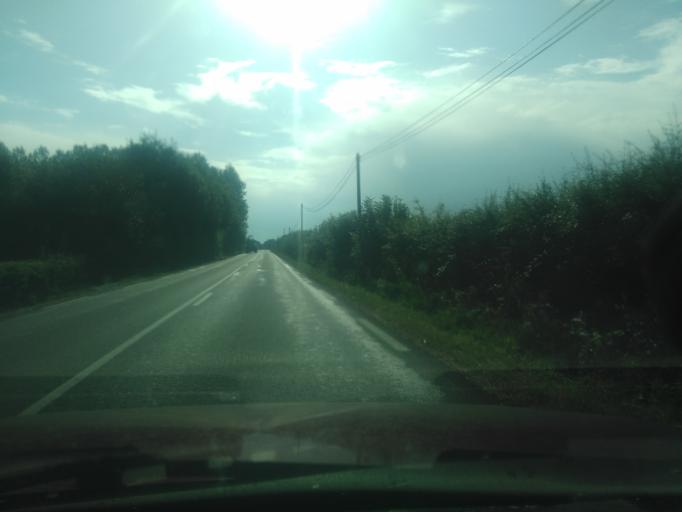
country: FR
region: Pays de la Loire
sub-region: Departement de la Vendee
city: Saint-Pierre-du-Chemin
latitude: 46.6518
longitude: -0.6730
